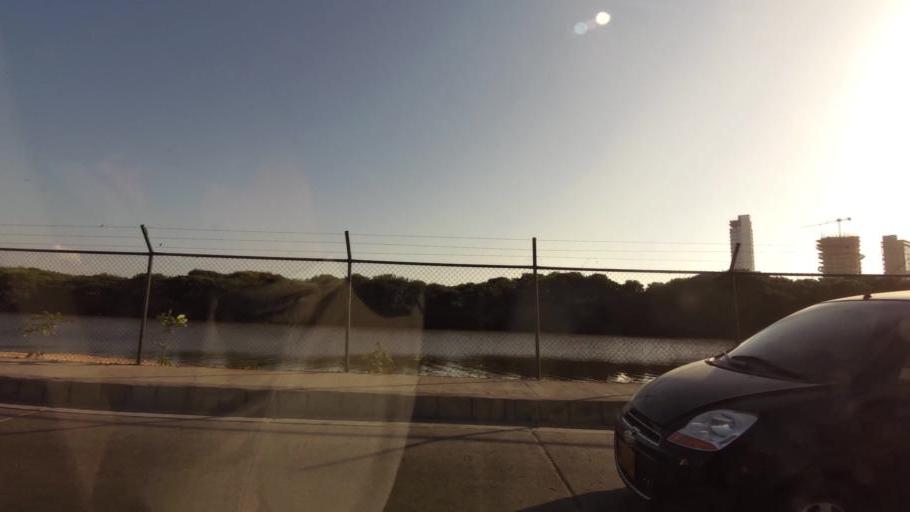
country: CO
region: Bolivar
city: Cartagena
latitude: 10.4127
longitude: -75.5292
